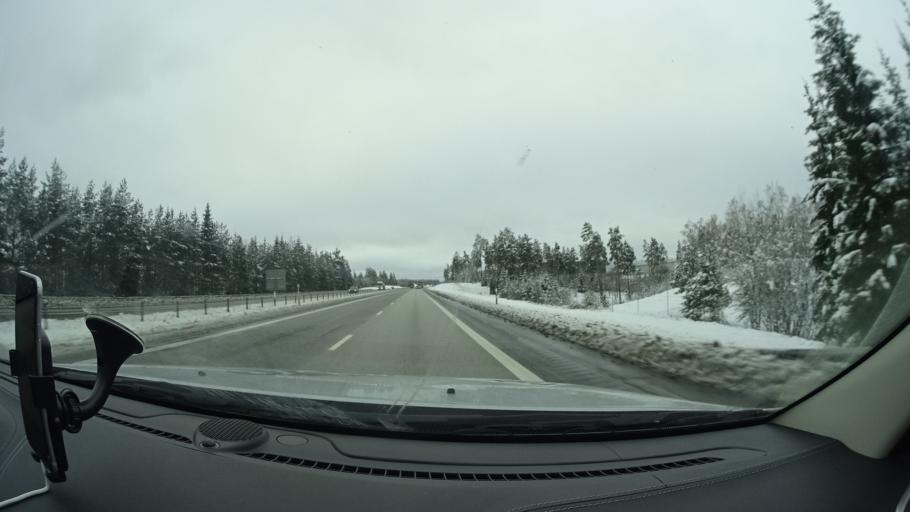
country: SE
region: Joenkoeping
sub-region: Jonkopings Kommun
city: Odensjo
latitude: 57.6746
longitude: 14.1709
